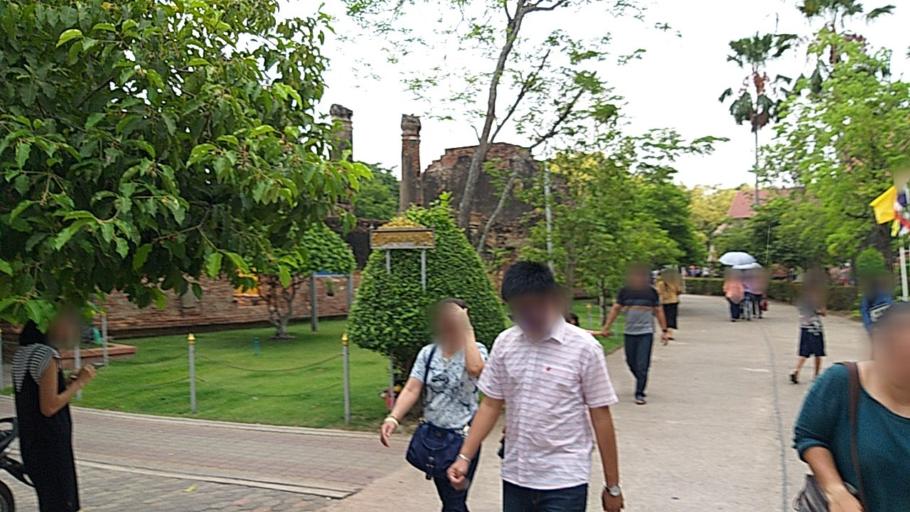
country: TH
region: Phra Nakhon Si Ayutthaya
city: Phra Nakhon Si Ayutthaya
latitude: 14.3462
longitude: 100.5929
